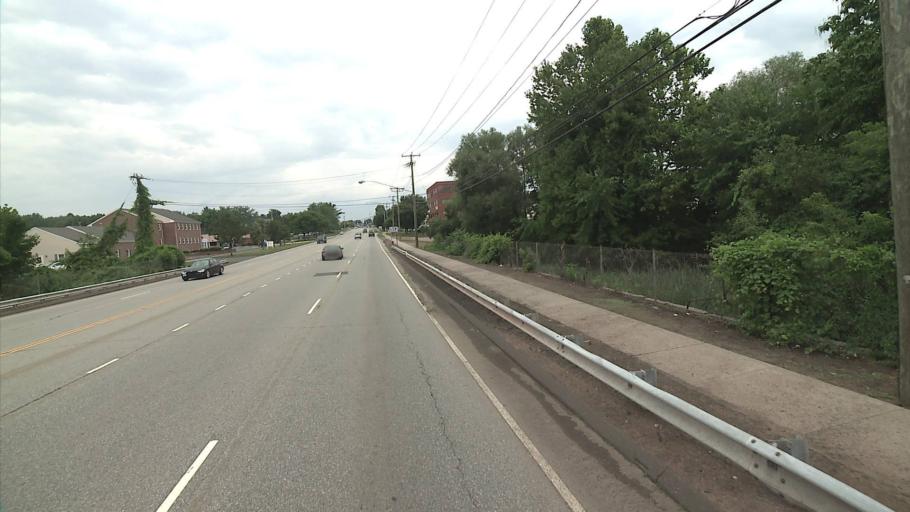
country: US
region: Connecticut
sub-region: Hartford County
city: Wethersfield
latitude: 41.6887
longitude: -72.6554
